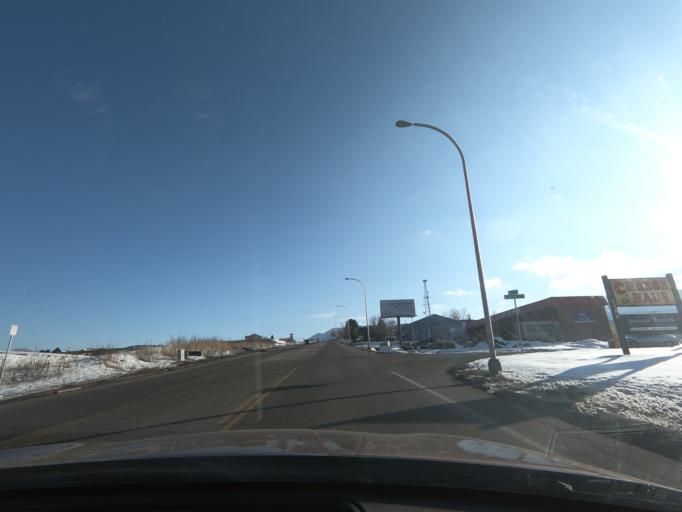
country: US
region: Colorado
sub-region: El Paso County
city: Colorado Springs
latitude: 38.8345
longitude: -104.8592
